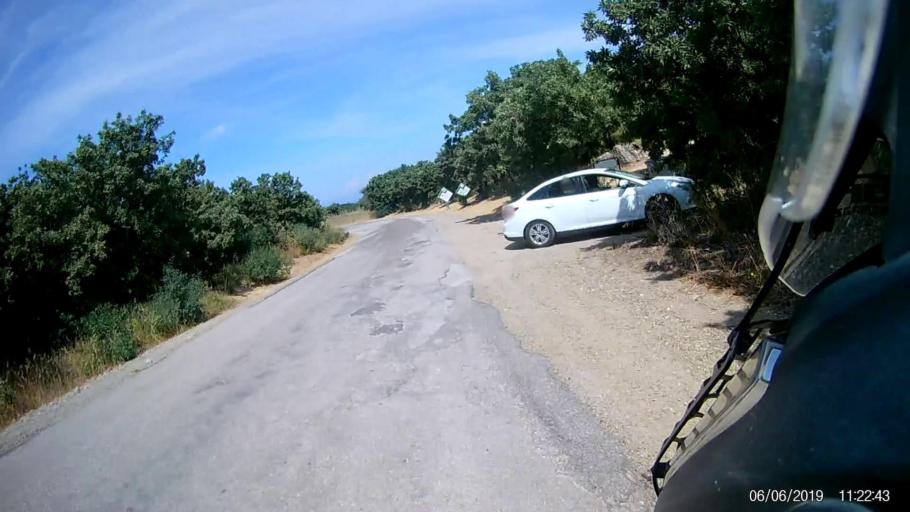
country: TR
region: Canakkale
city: Gulpinar
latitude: 39.6117
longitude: 26.1840
